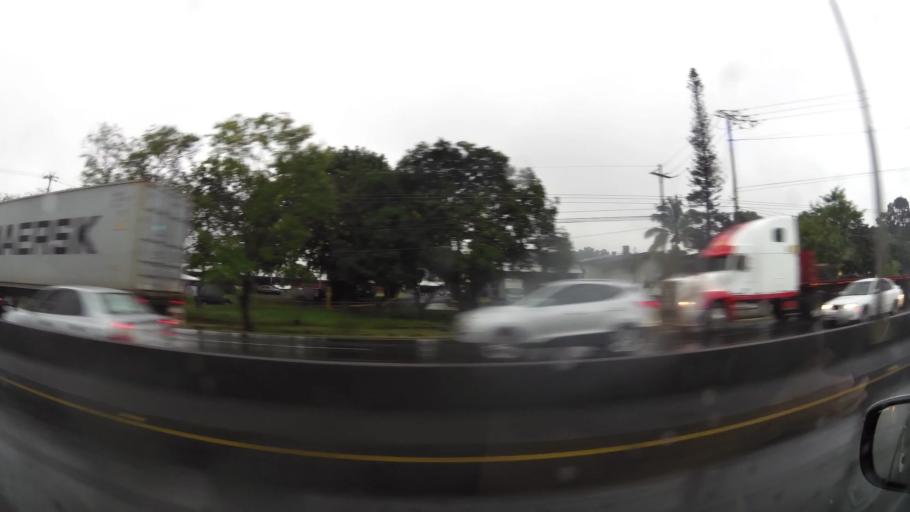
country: CR
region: Heredia
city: Llorente
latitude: 10.0000
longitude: -84.1722
